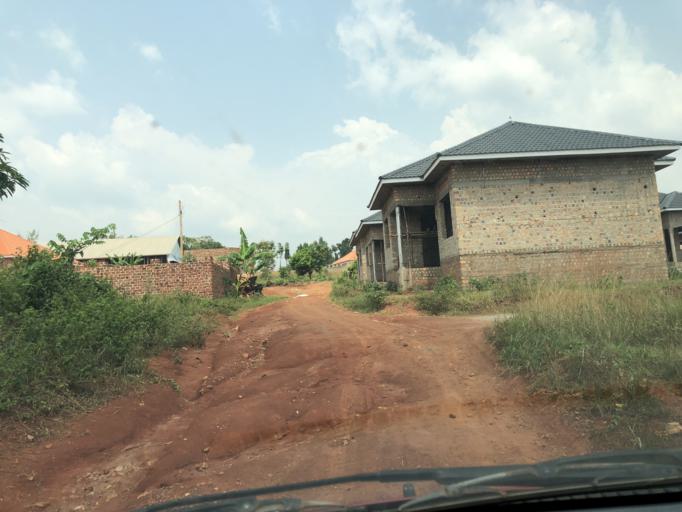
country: UG
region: Central Region
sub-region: Wakiso District
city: Bweyogerere
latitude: 0.4740
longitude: 32.6373
